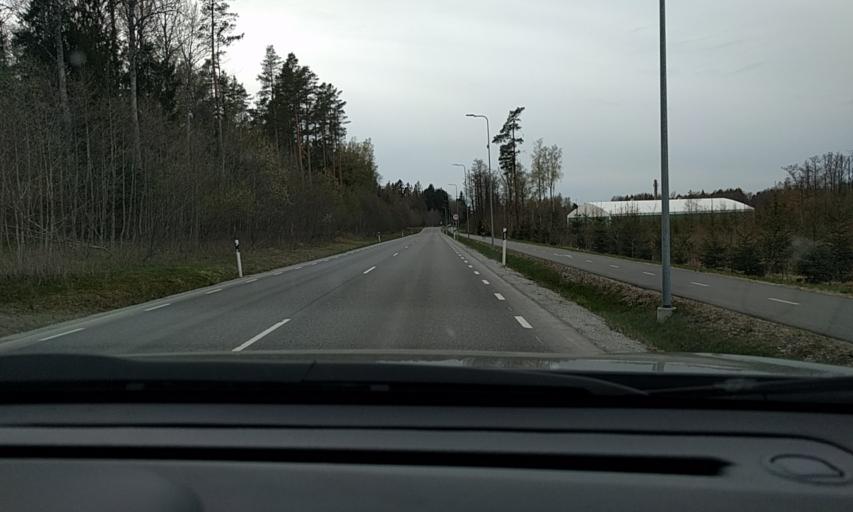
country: EE
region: Harju
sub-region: Viimsi vald
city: Viimsi
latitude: 59.5259
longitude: 24.8828
